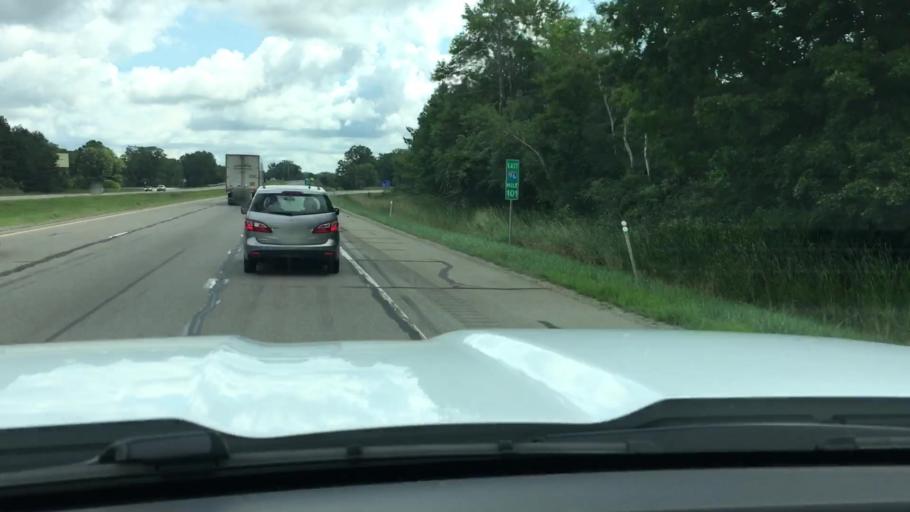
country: US
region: Michigan
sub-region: Eaton County
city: Dimondale
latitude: 42.6653
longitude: -84.5972
